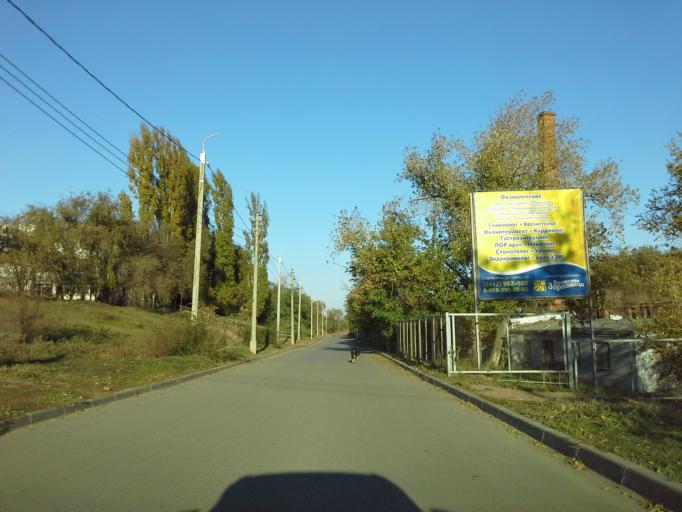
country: RU
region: Volgograd
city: Vodstroy
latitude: 48.8197
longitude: 44.6400
